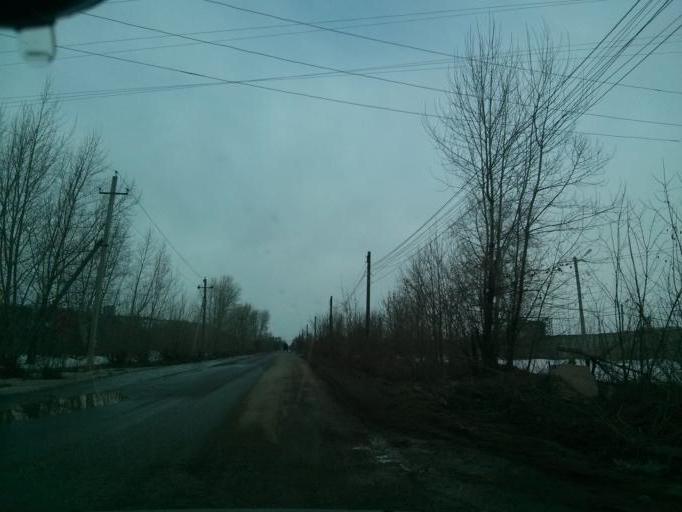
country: RU
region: Nizjnij Novgorod
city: Afonino
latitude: 56.2902
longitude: 44.1143
